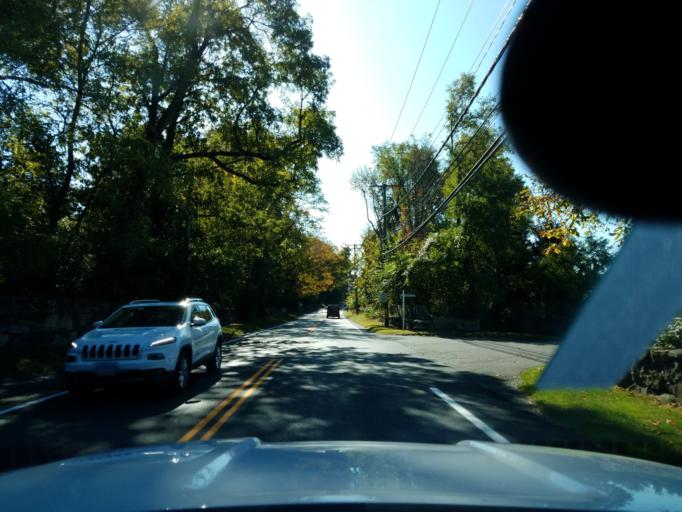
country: US
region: Connecticut
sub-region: Fairfield County
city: Cos Cob
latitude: 41.0638
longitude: -73.6195
